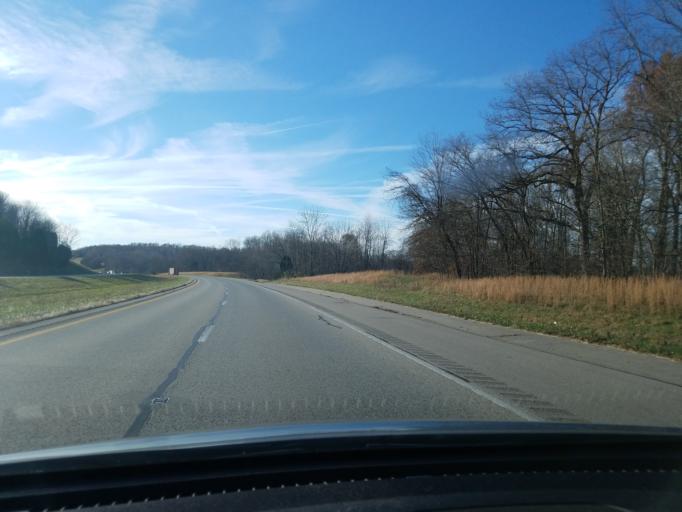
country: US
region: Indiana
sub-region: Crawford County
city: English
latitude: 38.2550
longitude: -86.3047
